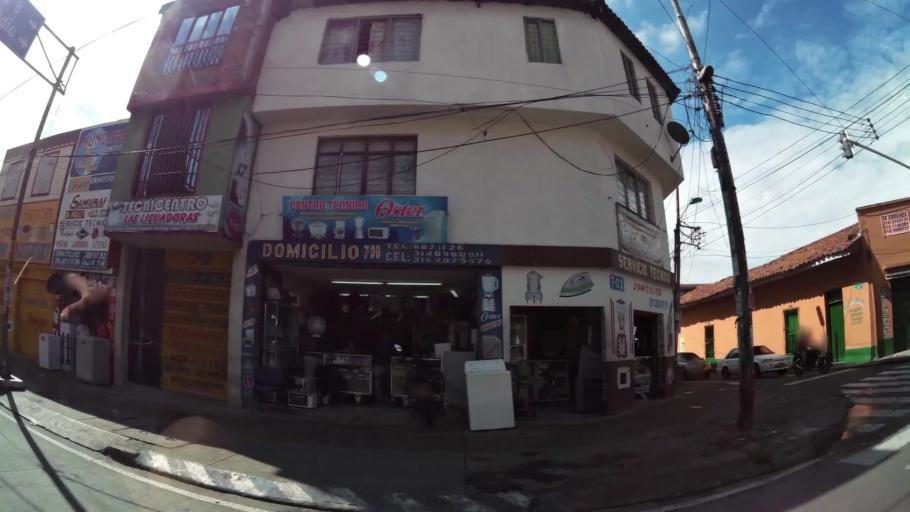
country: CO
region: Valle del Cauca
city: Cali
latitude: 3.4466
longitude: -76.5348
